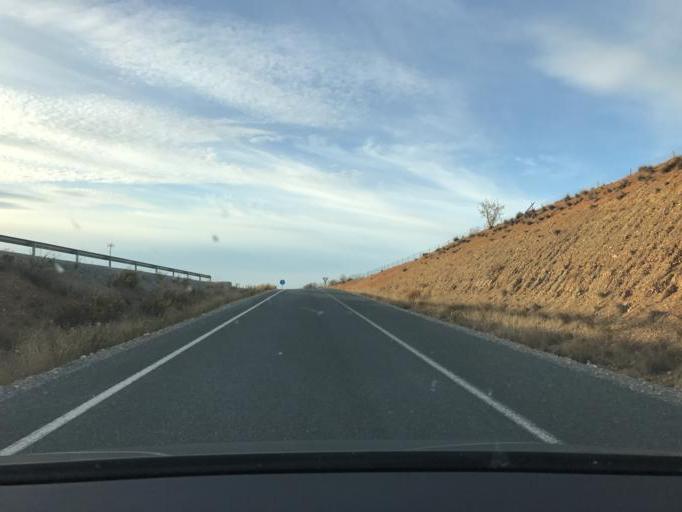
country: ES
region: Andalusia
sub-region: Provincia de Granada
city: Albunan
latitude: 37.2629
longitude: -3.0855
